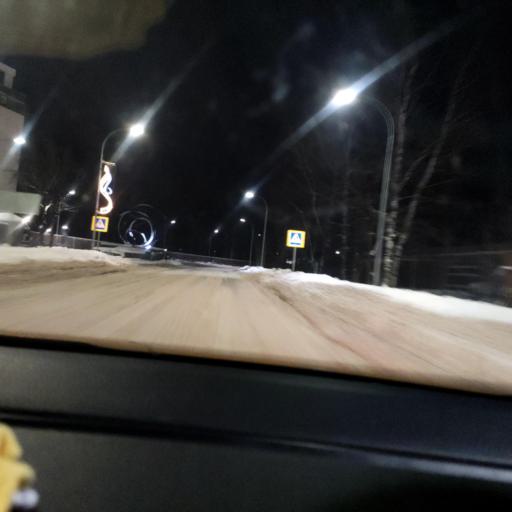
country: RU
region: Moskovskaya
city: Krasnogorsk
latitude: 55.8772
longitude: 37.3130
